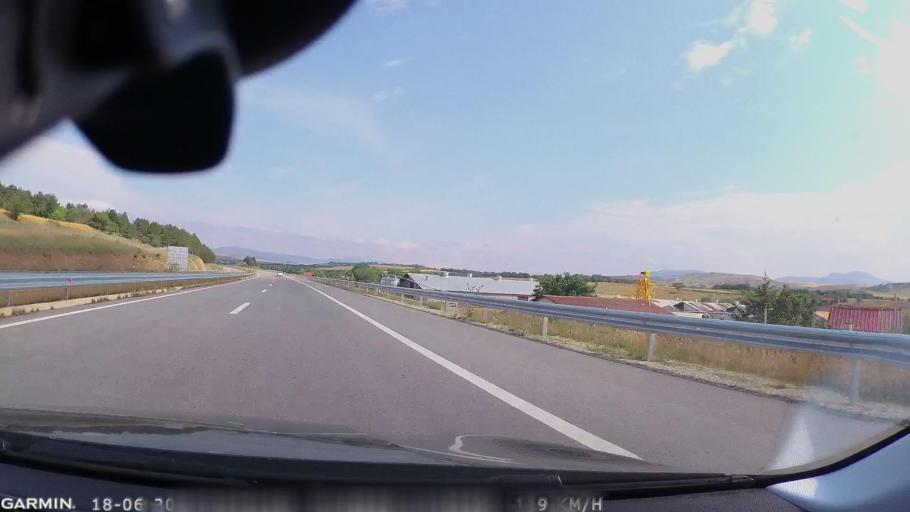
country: MK
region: Sveti Nikole
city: Sveti Nikole
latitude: 41.8840
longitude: 21.9344
